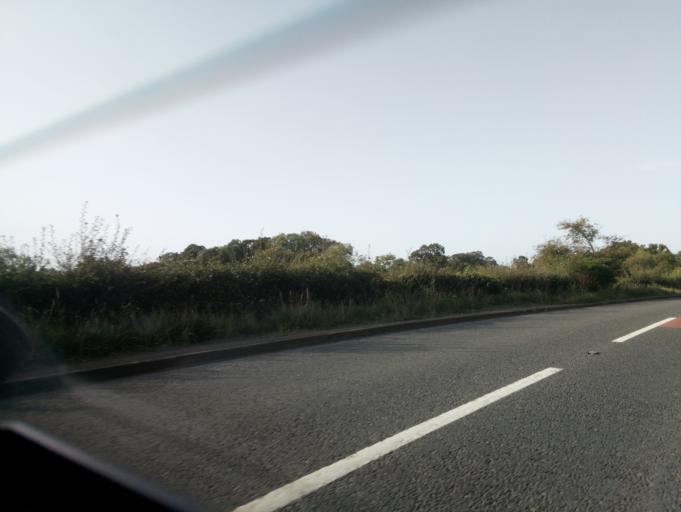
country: GB
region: England
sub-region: Gloucestershire
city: Gloucester
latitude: 51.9089
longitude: -2.2955
